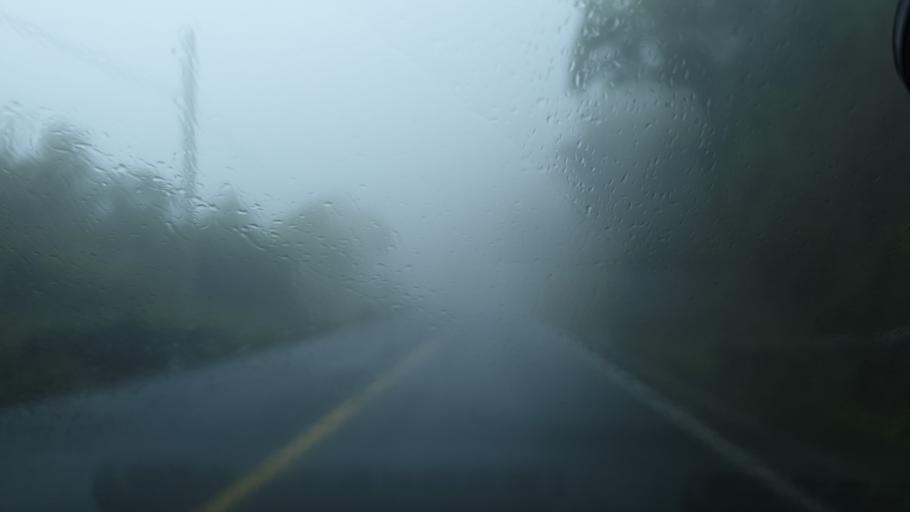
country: EC
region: Manabi
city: Jipijapa
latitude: -1.3474
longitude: -80.6544
